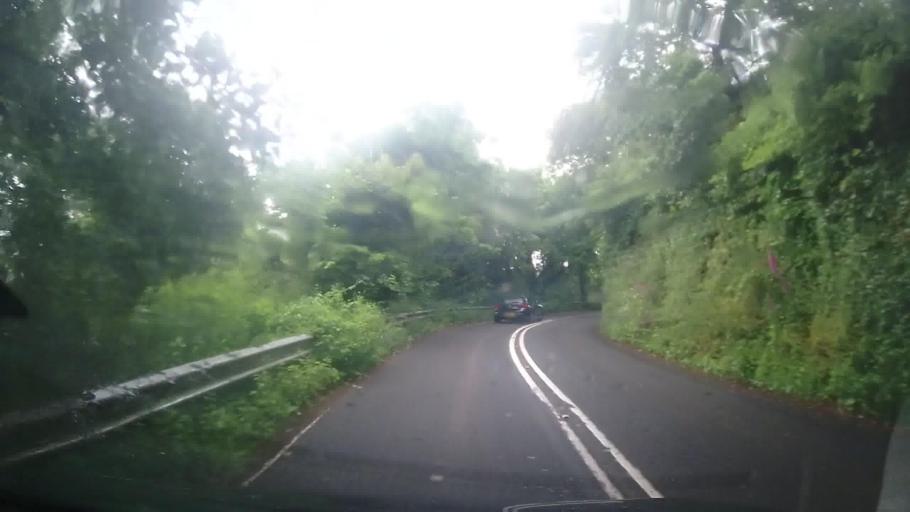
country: GB
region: England
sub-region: Devon
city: Dartmouth
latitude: 50.3661
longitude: -3.5702
